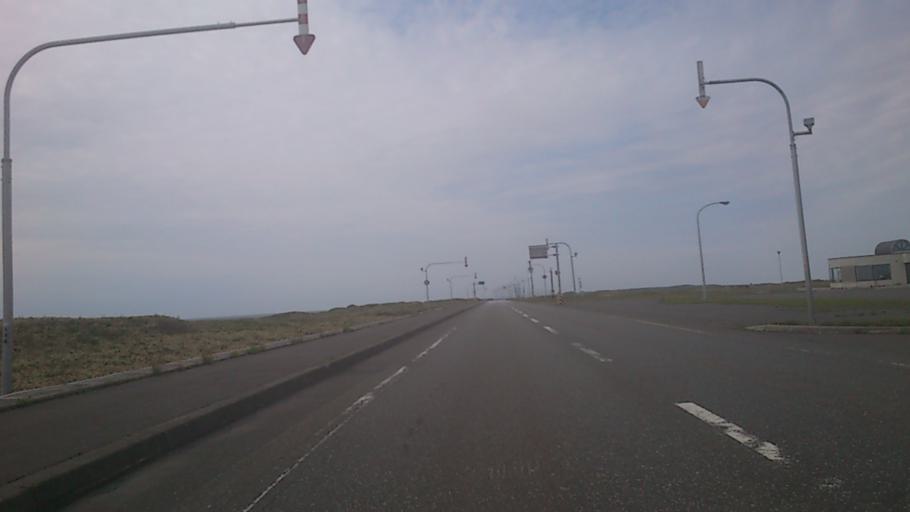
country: JP
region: Hokkaido
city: Makubetsu
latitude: 44.9244
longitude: 141.7223
